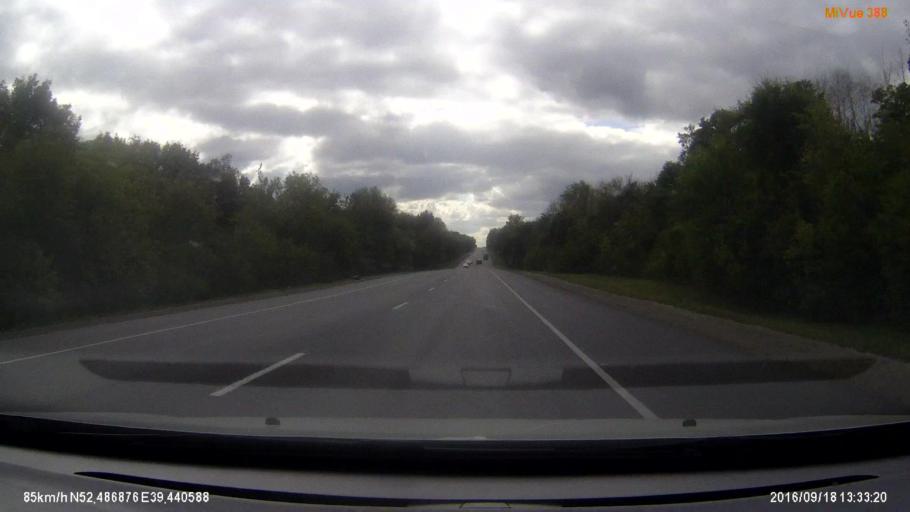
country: RU
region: Lipetsk
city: Borinskoye
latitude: 52.4767
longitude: 39.4279
